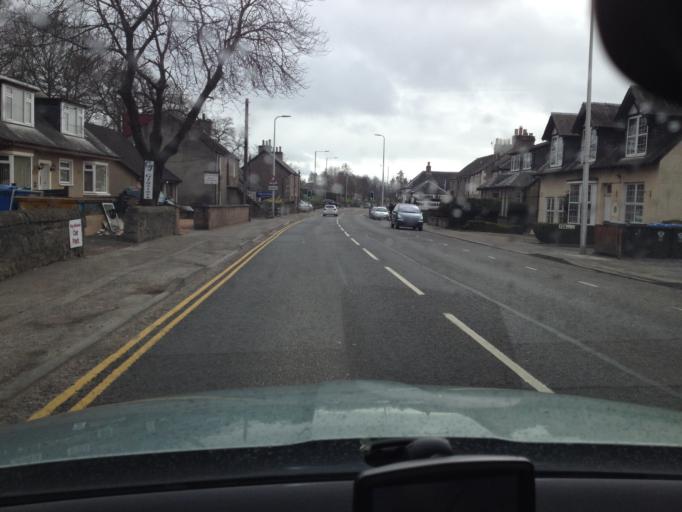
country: GB
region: Scotland
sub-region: Perth and Kinross
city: Scone
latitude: 56.4159
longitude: -3.4039
